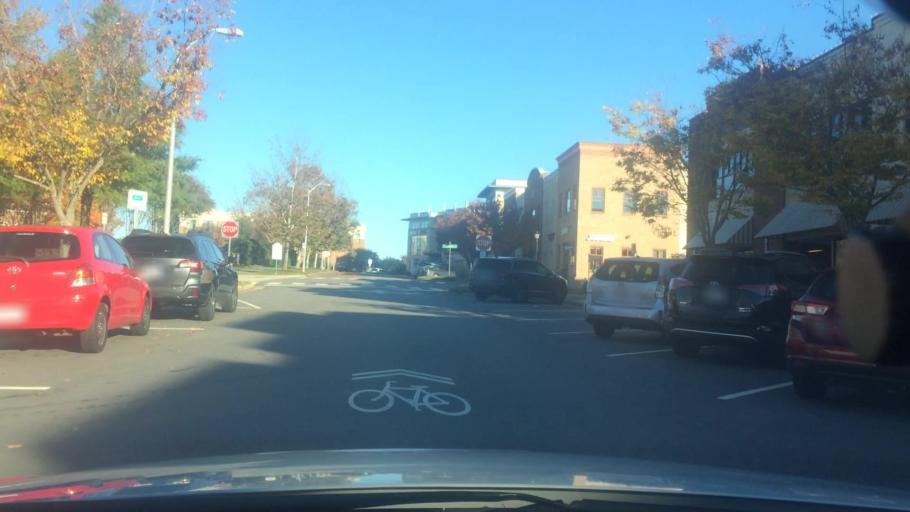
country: US
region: North Carolina
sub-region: Orange County
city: Carrboro
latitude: 35.8806
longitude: -79.0654
